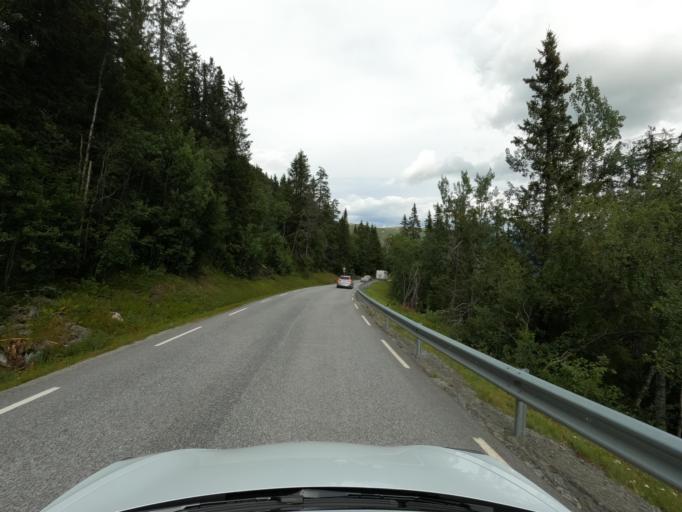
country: NO
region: Telemark
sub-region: Tinn
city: Rjukan
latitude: 59.8644
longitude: 8.4711
